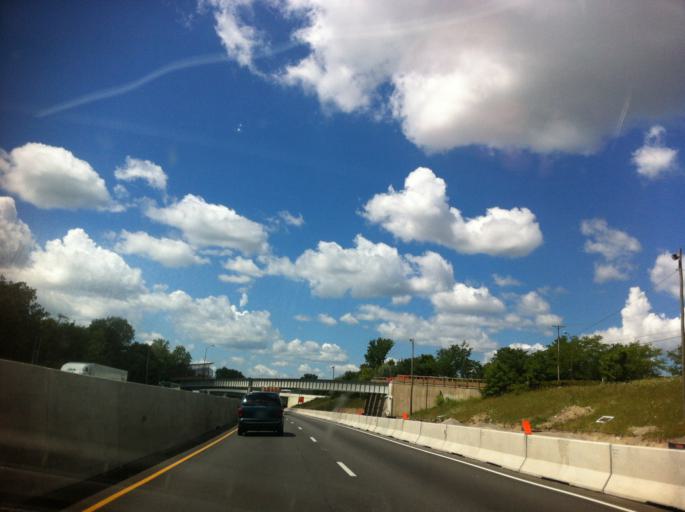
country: US
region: Ohio
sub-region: Lucas County
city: Toledo
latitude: 41.6558
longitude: -83.5566
